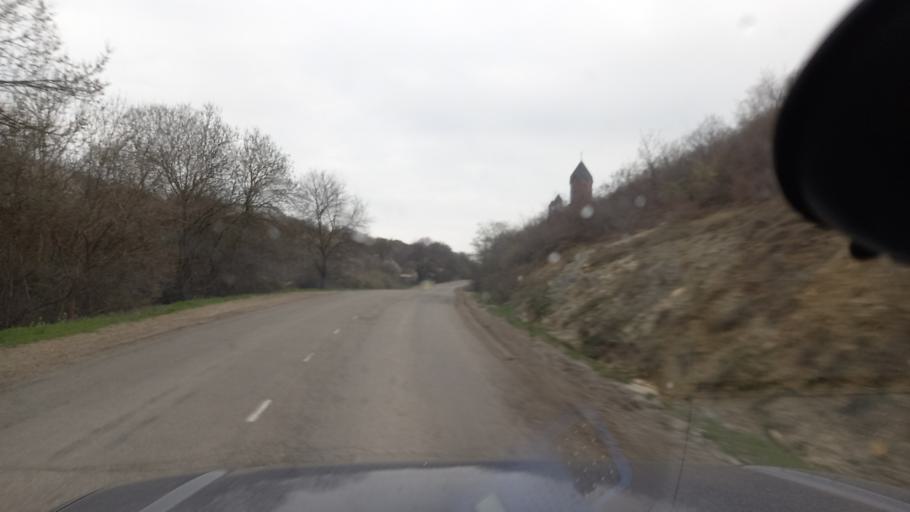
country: RU
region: Krasnodarskiy
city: Sukko
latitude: 44.8448
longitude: 37.4346
